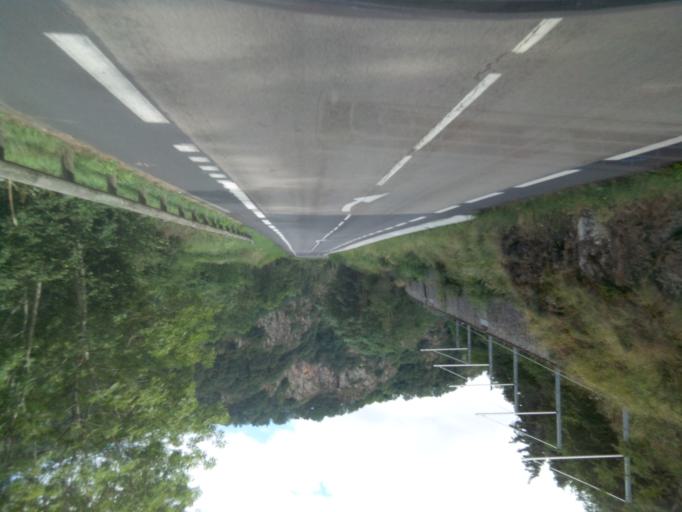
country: FR
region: Auvergne
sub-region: Departement de la Haute-Loire
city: Chadrac
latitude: 45.0879
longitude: 3.9109
